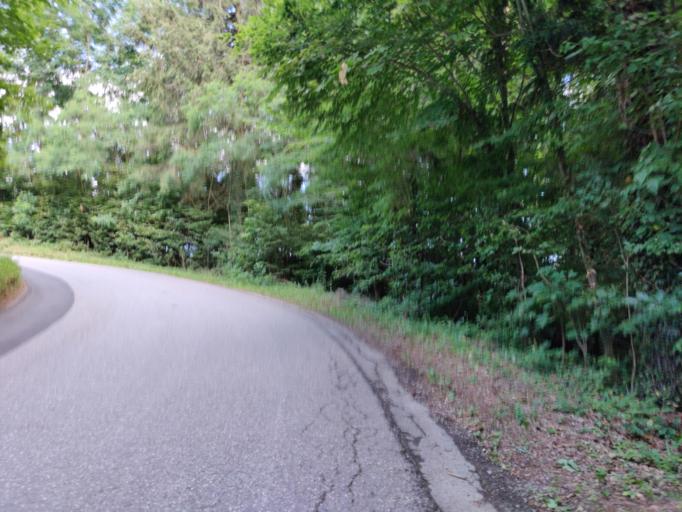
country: AT
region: Styria
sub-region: Politischer Bezirk Graz-Umgebung
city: Thal
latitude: 47.0742
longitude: 15.3394
